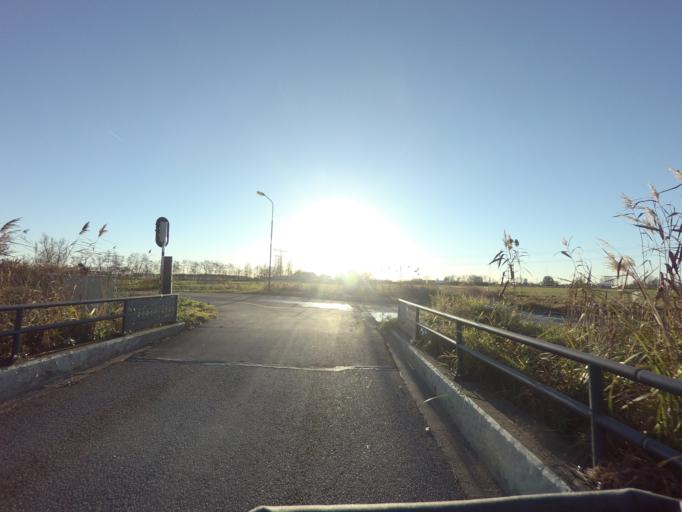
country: NL
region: Utrecht
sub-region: Stichtse Vecht
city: Spechtenkamp
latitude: 52.1526
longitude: 5.0022
